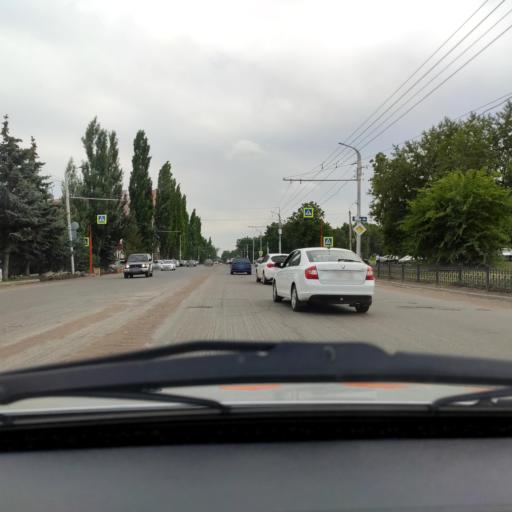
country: RU
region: Bashkortostan
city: Sterlitamak
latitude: 53.6535
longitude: 55.9479
